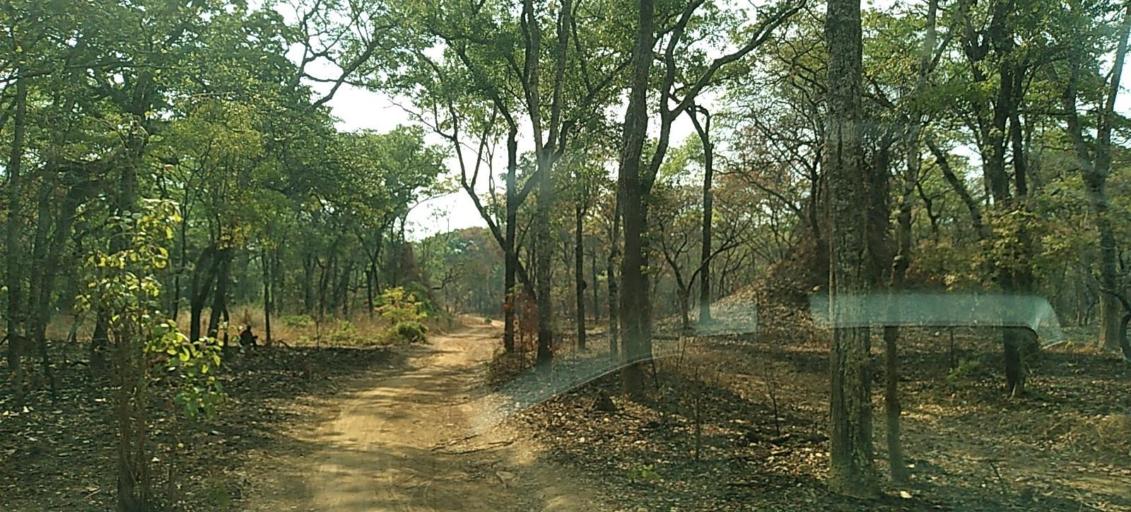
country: ZM
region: North-Western
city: Solwezi
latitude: -12.0694
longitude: 26.2235
